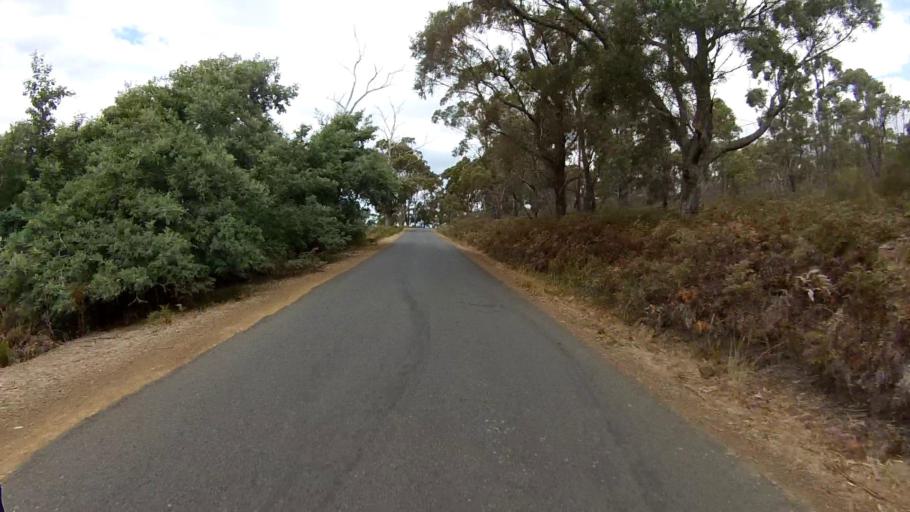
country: AU
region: Tasmania
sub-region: Sorell
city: Sorell
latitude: -42.5992
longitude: 147.9254
